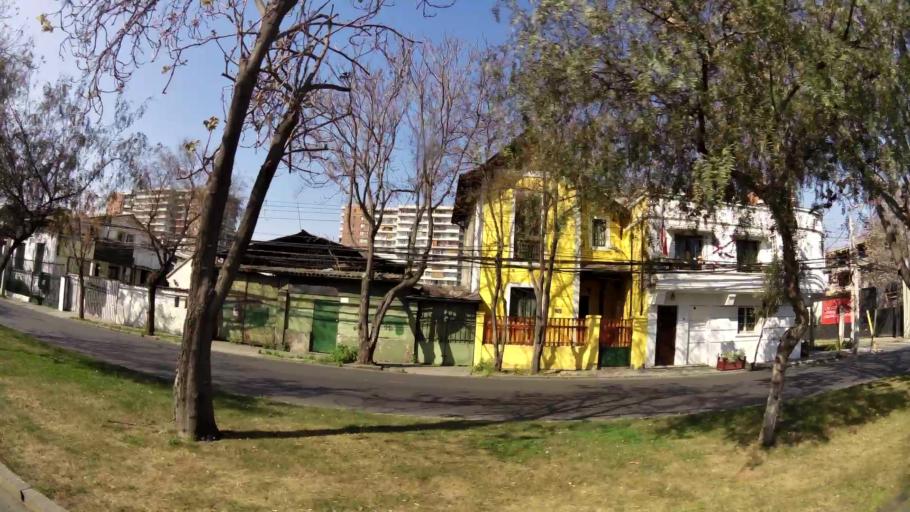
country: CL
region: Santiago Metropolitan
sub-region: Provincia de Santiago
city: Santiago
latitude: -33.4589
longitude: -70.6264
